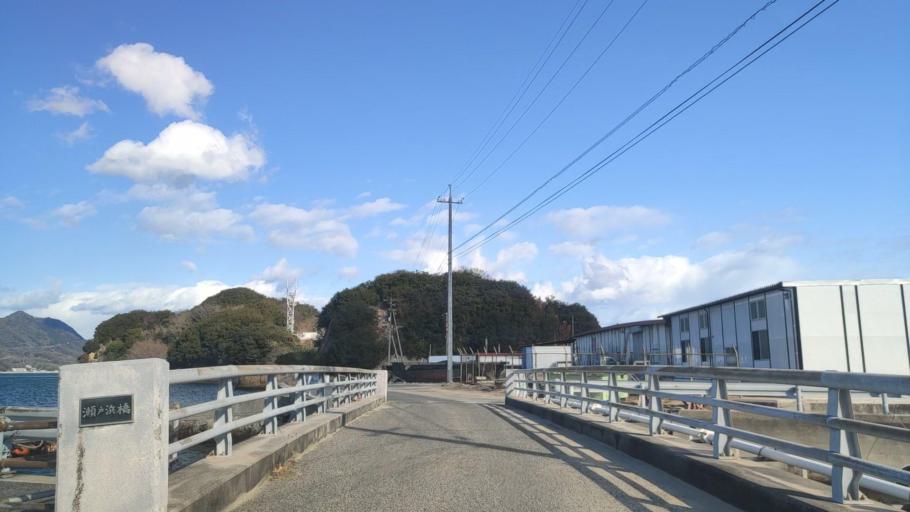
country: JP
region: Hiroshima
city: Innoshima
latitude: 34.2161
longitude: 133.1214
